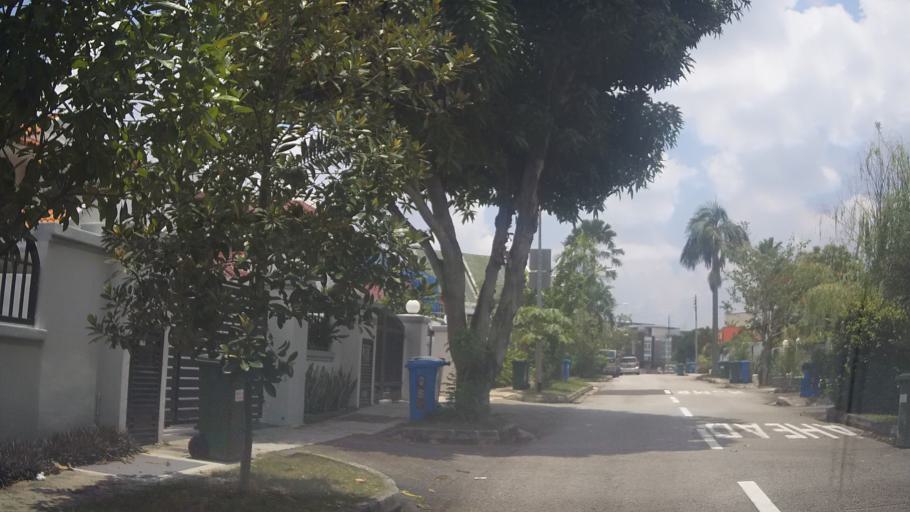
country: SG
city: Singapore
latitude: 1.3604
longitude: 103.8718
